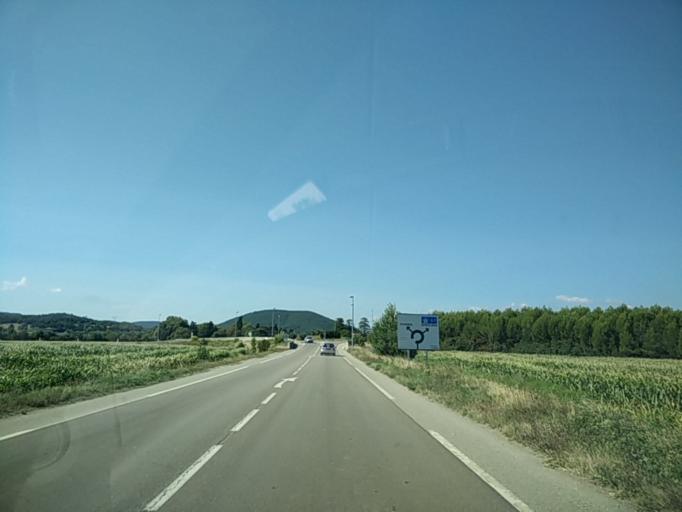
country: FR
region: Rhone-Alpes
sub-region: Departement de la Drome
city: Montboucher-sur-Jabron
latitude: 44.5491
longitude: 4.8284
